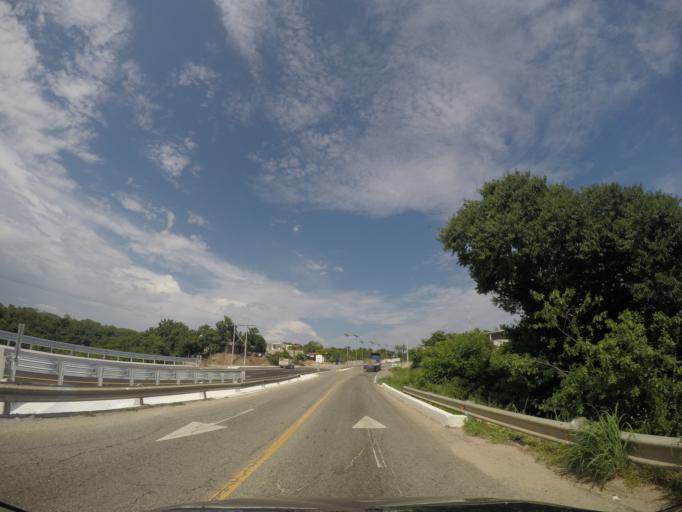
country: MX
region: Oaxaca
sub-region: Santa Maria Colotepec
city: Brisas de Zicatela
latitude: 15.8275
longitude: -97.0253
